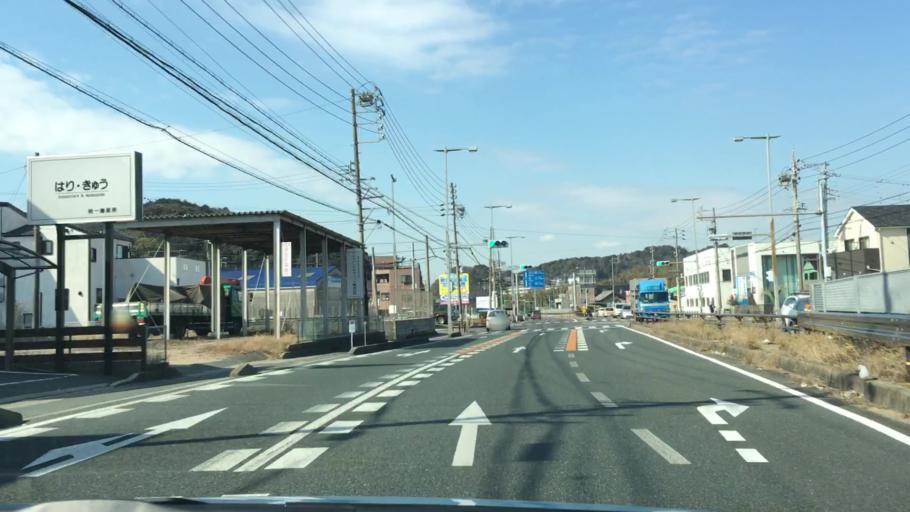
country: JP
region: Aichi
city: Gamagori
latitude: 34.8953
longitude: 137.2529
